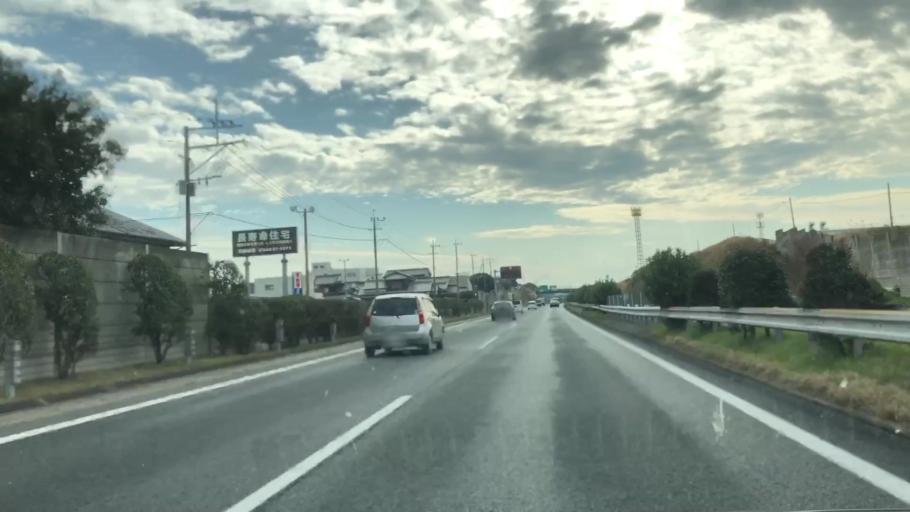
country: JP
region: Fukuoka
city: Kurume
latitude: 33.2612
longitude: 130.5383
